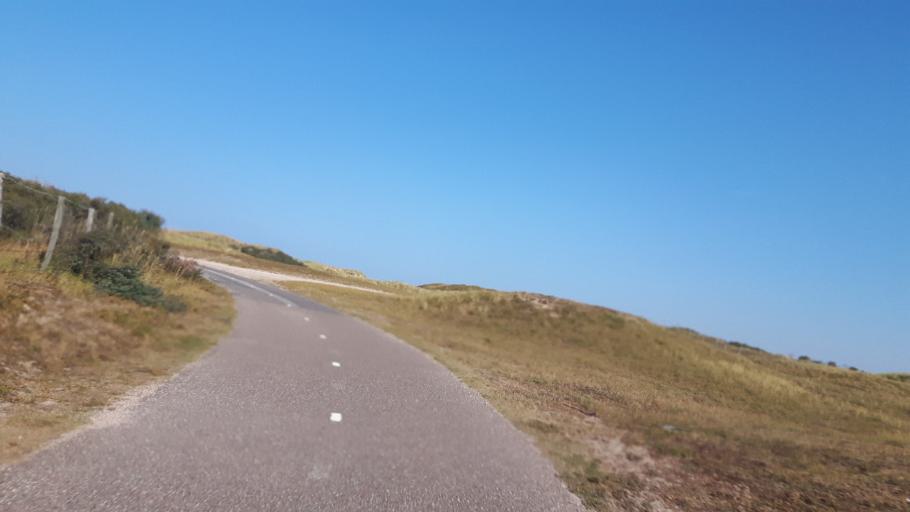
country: NL
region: North Holland
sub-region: Gemeente Zandvoort
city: Zandvoort
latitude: 52.3476
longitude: 4.5118
